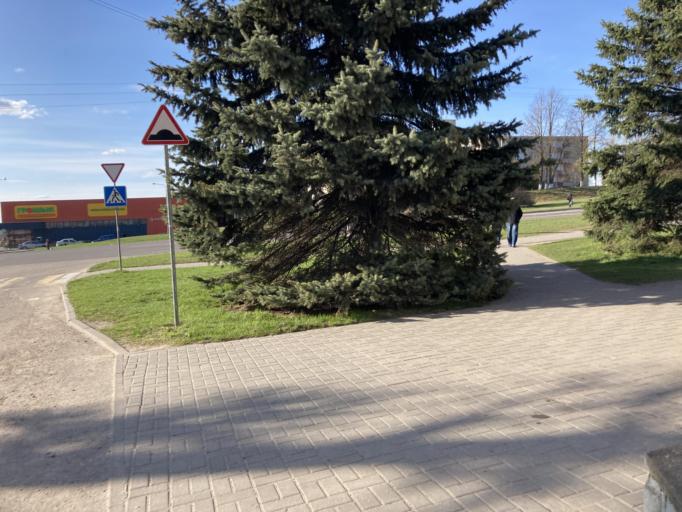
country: BY
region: Grodnenskaya
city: Slonim
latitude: 53.0862
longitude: 25.3038
